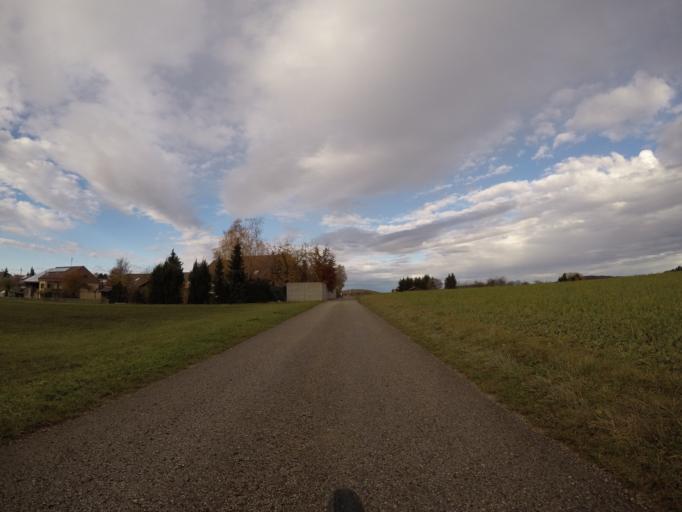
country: DE
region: Baden-Wuerttemberg
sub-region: Tuebingen Region
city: Sankt Johann
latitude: 48.4356
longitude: 9.3259
